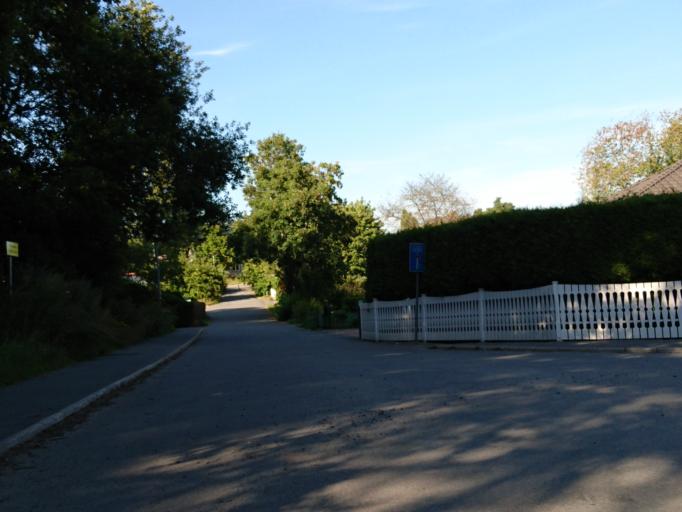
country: SE
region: Stockholm
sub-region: Huddinge Kommun
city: Segeltorp
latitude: 59.2735
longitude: 17.9467
